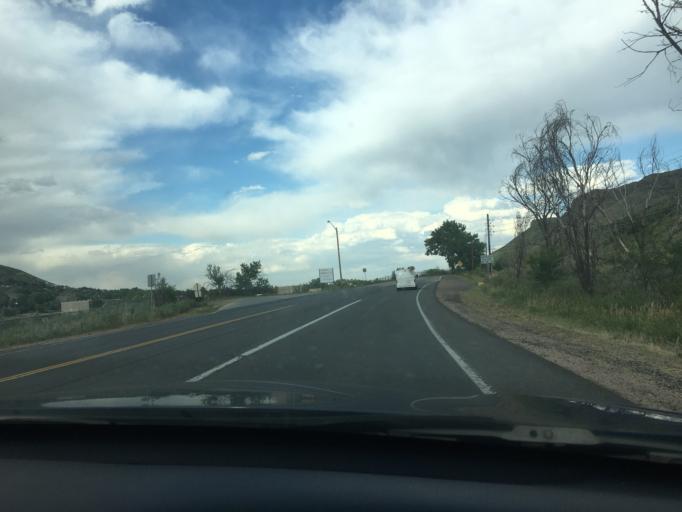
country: US
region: Colorado
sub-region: Jefferson County
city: Golden
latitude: 39.7629
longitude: -105.2095
